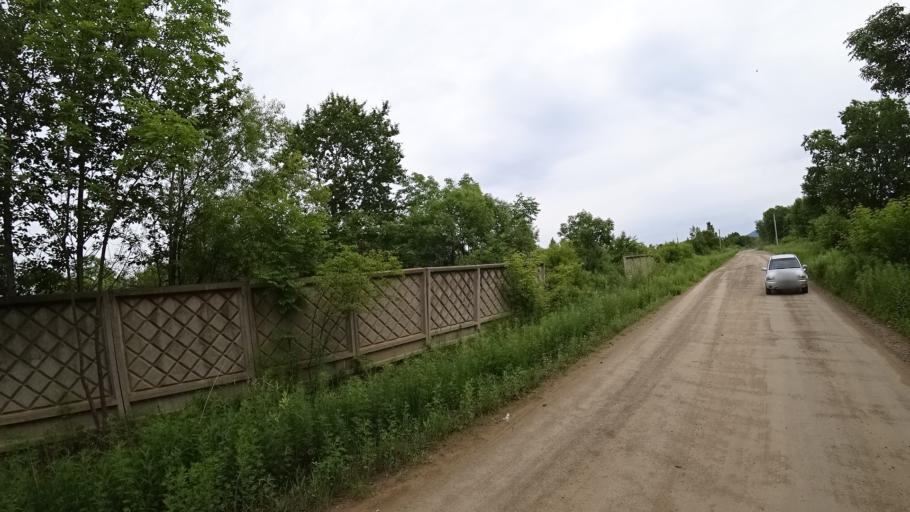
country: RU
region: Primorskiy
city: Arsen'yev
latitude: 44.1962
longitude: 133.3081
